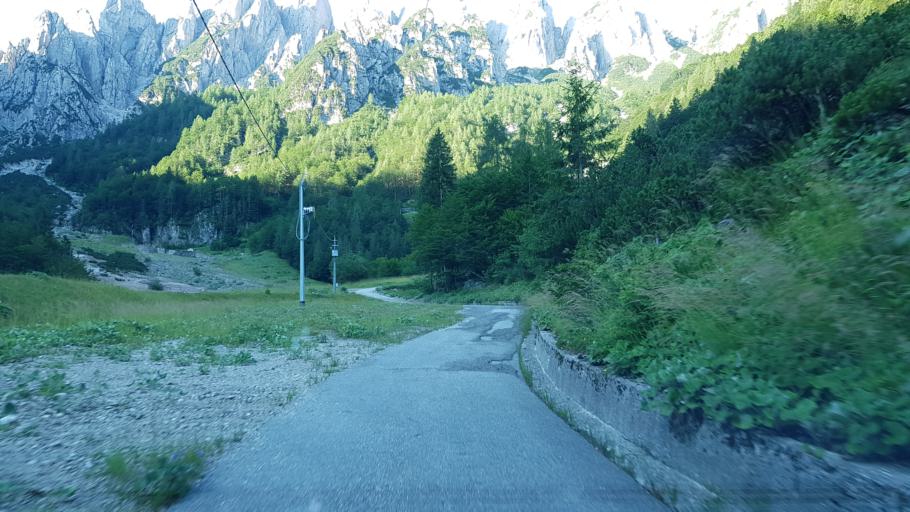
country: IT
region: Friuli Venezia Giulia
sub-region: Provincia di Udine
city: Pontebba
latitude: 46.4846
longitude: 13.2533
